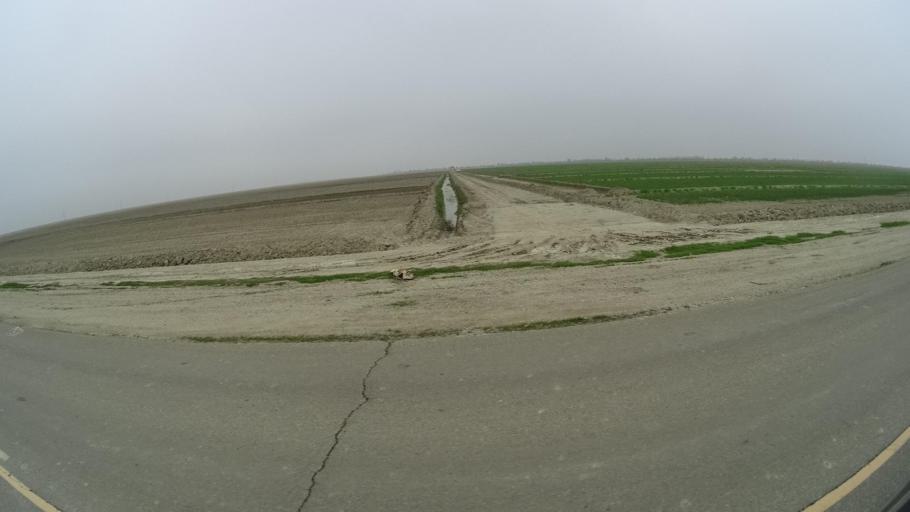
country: US
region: California
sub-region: Kern County
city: Rosedale
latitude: 35.2348
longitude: -119.2528
